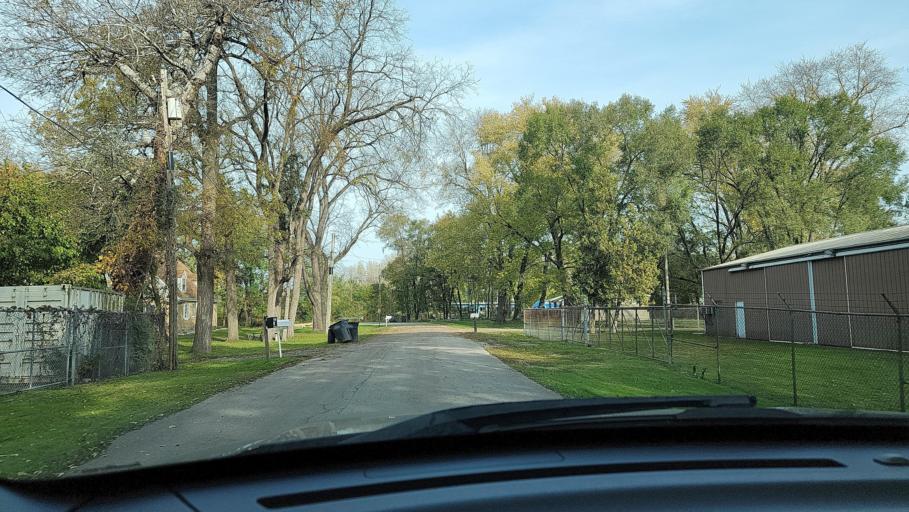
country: US
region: Indiana
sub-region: Porter County
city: Ogden Dunes
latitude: 41.6108
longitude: -87.1725
